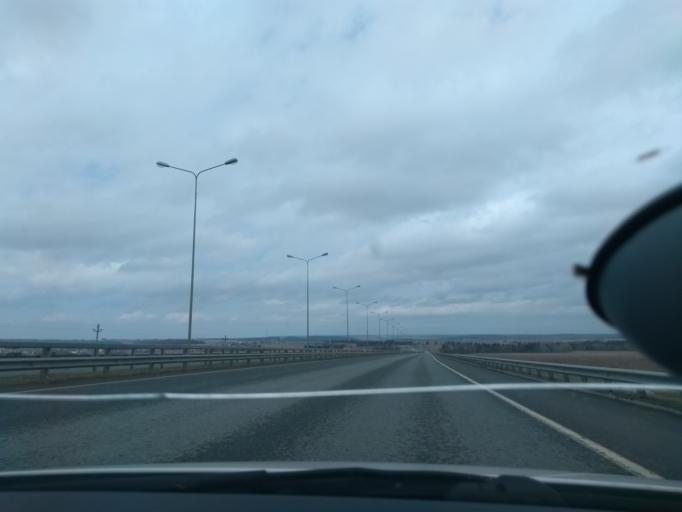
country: RU
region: Perm
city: Zvezdnyy
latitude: 57.7687
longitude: 56.3354
